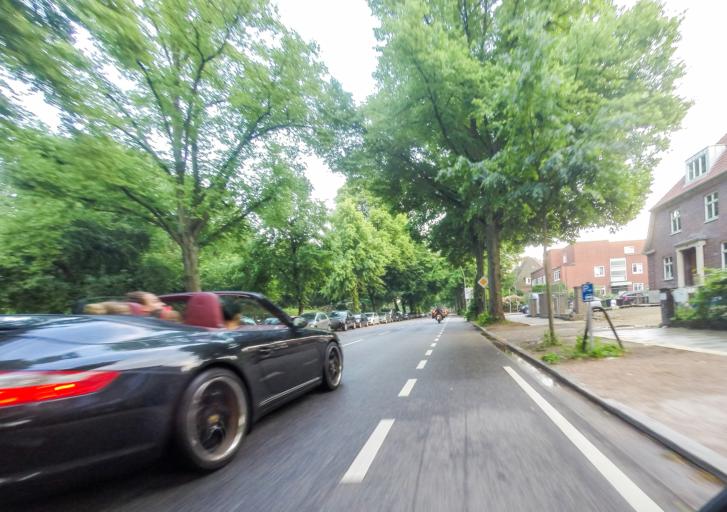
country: DE
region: Hamburg
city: Winterhude
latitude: 53.5964
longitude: 9.9946
